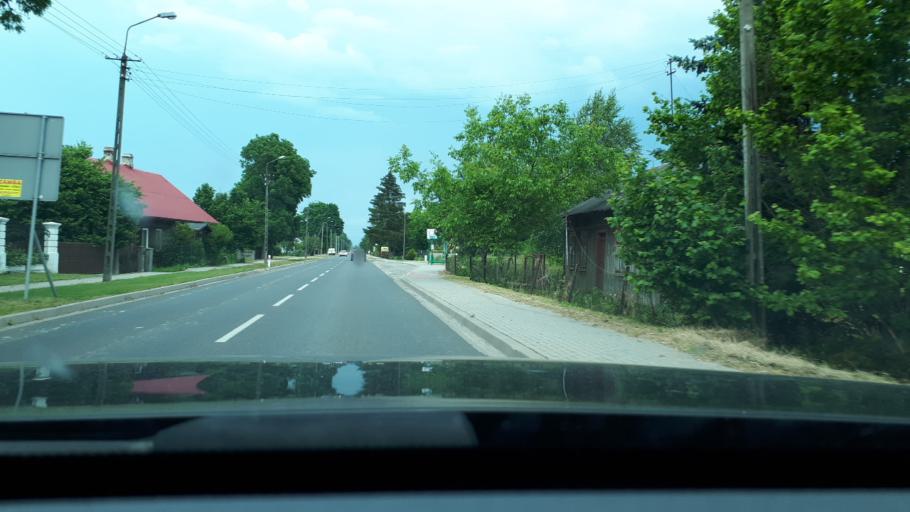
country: PL
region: Masovian Voivodeship
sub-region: Powiat warszawski zachodni
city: Kampinos
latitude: 52.2611
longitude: 20.5015
